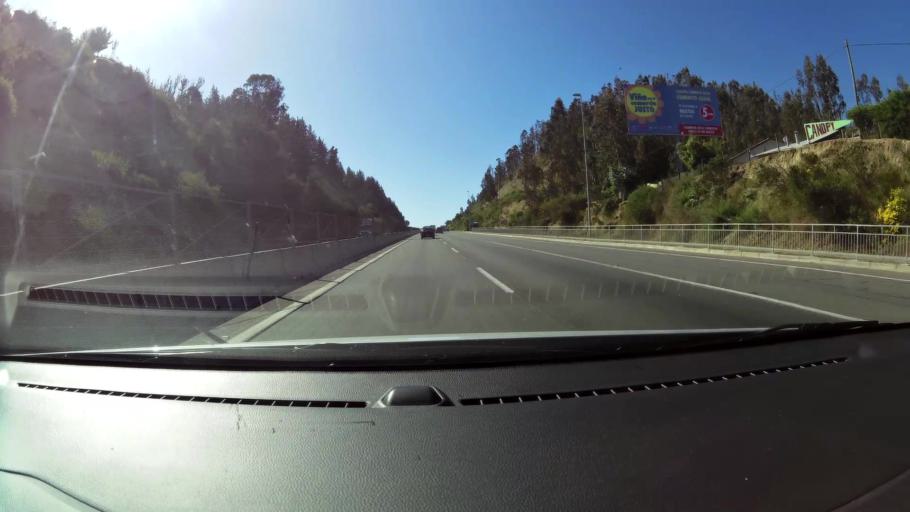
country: CL
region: Valparaiso
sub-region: Provincia de Marga Marga
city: Quilpue
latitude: -33.2079
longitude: -71.4815
